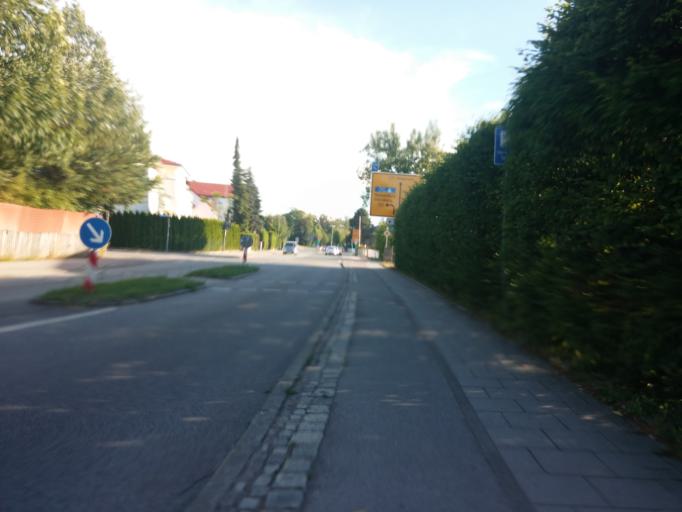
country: DE
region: Bavaria
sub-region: Upper Bavaria
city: Haar
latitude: 48.1075
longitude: 11.7374
